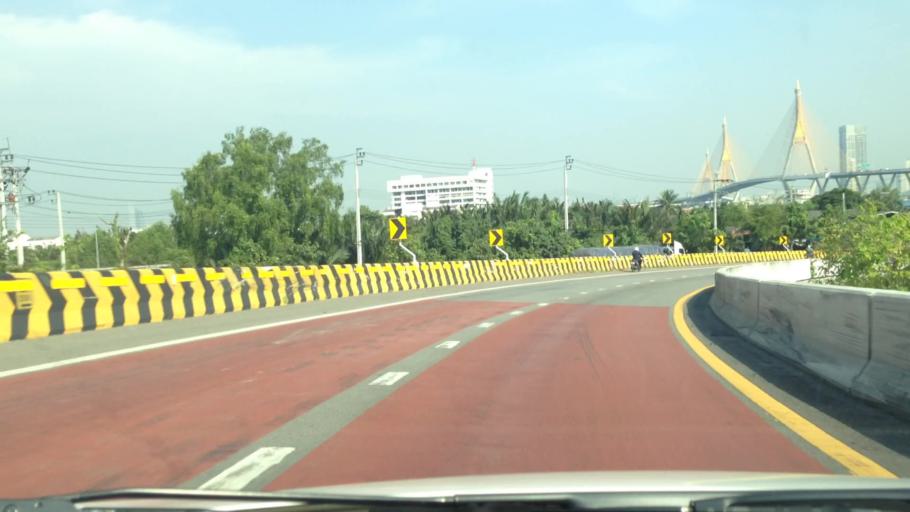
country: TH
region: Samut Prakan
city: Phra Pradaeng
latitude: 13.6472
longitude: 100.5395
